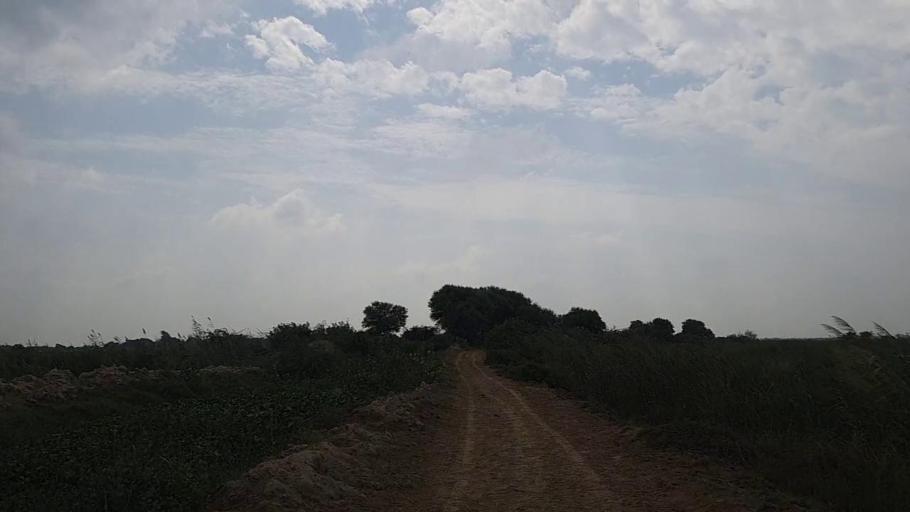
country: PK
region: Sindh
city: Mirpur Batoro
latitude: 24.6159
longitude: 68.1359
